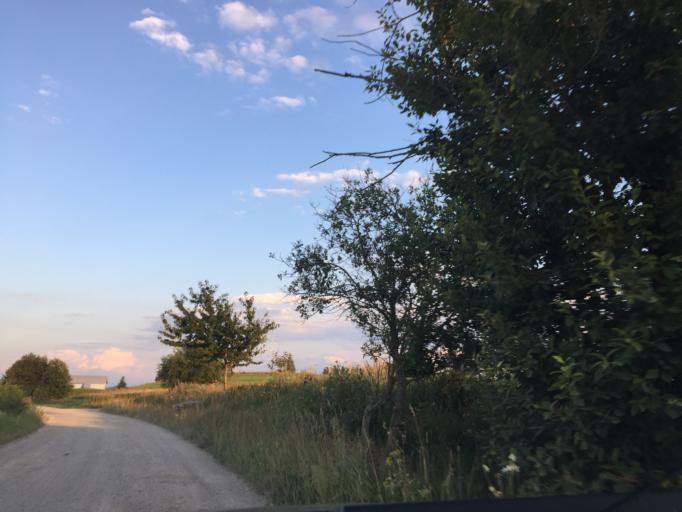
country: PL
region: Silesian Voivodeship
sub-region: Powiat zywiecki
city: Korbielow
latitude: 49.4884
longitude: 19.3577
